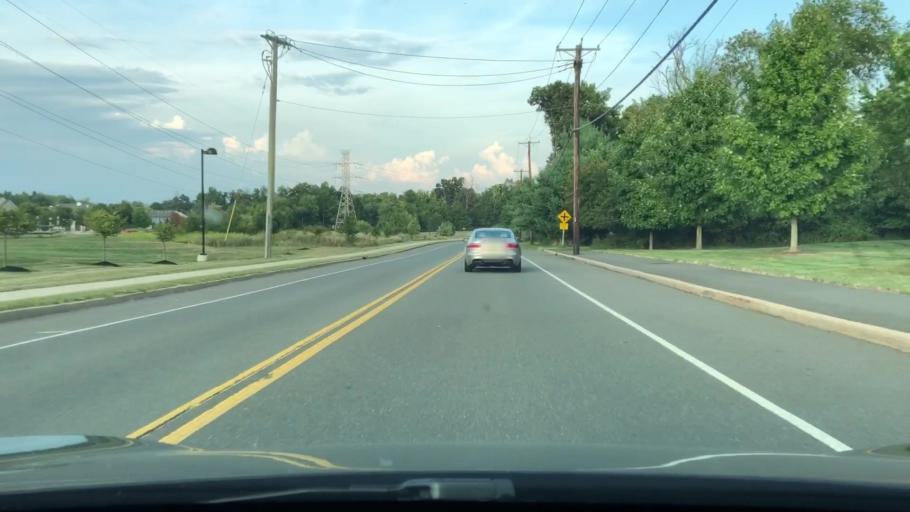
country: US
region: New Jersey
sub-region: Mercer County
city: Pennington
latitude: 40.3014
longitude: -74.7776
